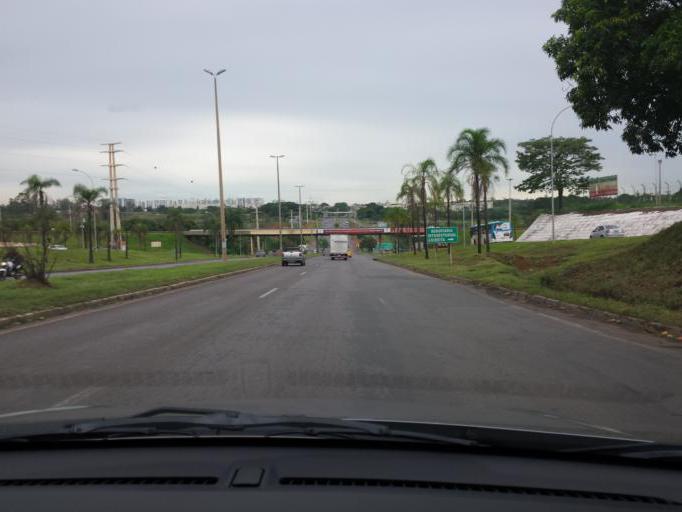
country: BR
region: Federal District
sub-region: Brasilia
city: Brasilia
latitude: -15.8495
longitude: -47.9546
